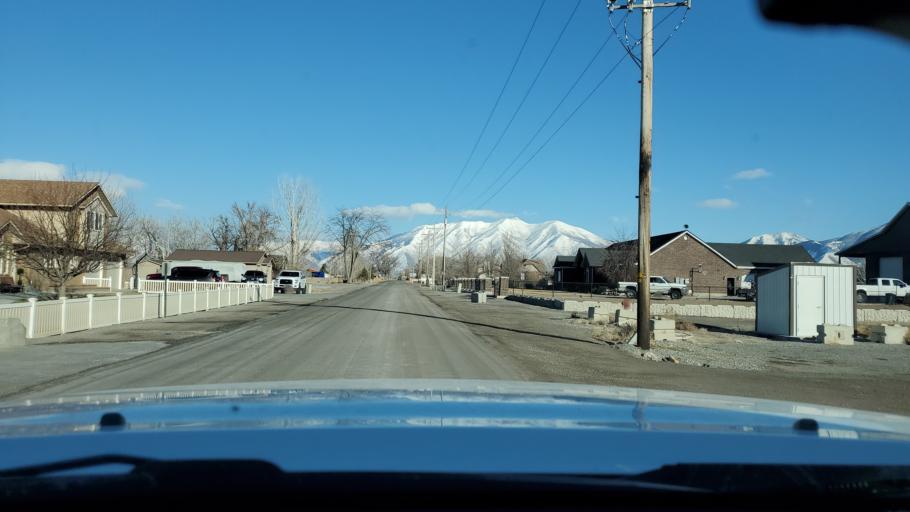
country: US
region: Utah
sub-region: Utah County
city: Benjamin
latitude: 40.1146
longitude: -111.7371
